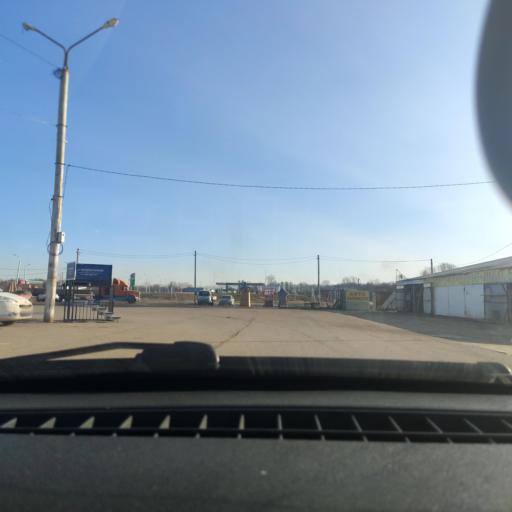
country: RU
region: Bashkortostan
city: Ufa
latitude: 54.8063
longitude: 56.1737
